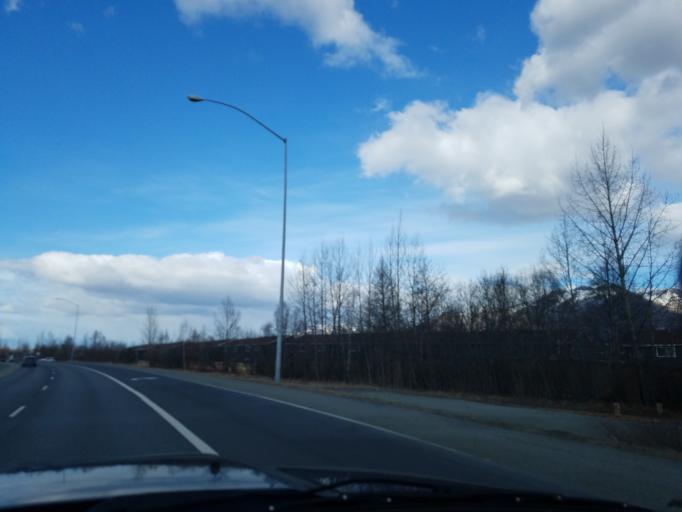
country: US
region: Alaska
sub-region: Anchorage Municipality
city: Elmendorf Air Force Base
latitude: 61.1839
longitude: -149.7348
